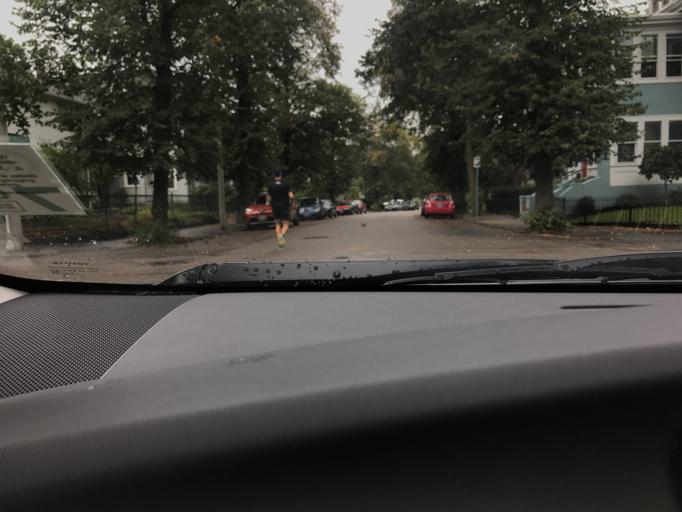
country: US
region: Massachusetts
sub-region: Suffolk County
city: Jamaica Plain
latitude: 42.3200
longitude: -71.1154
